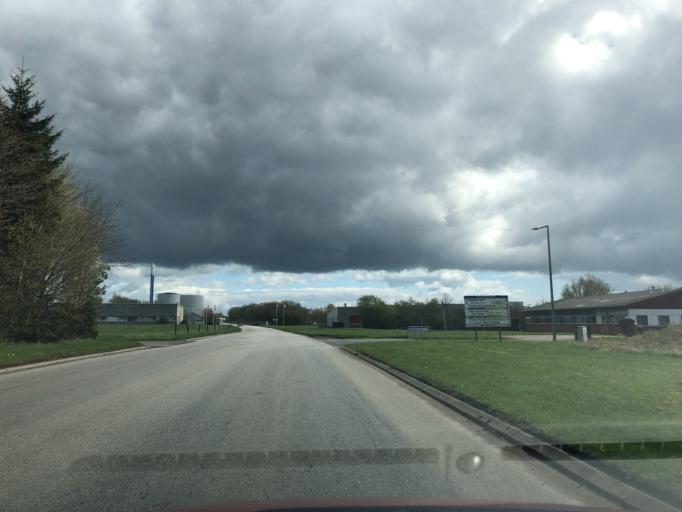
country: DK
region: South Denmark
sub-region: Kolding Kommune
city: Christiansfeld
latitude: 55.3639
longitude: 9.4852
